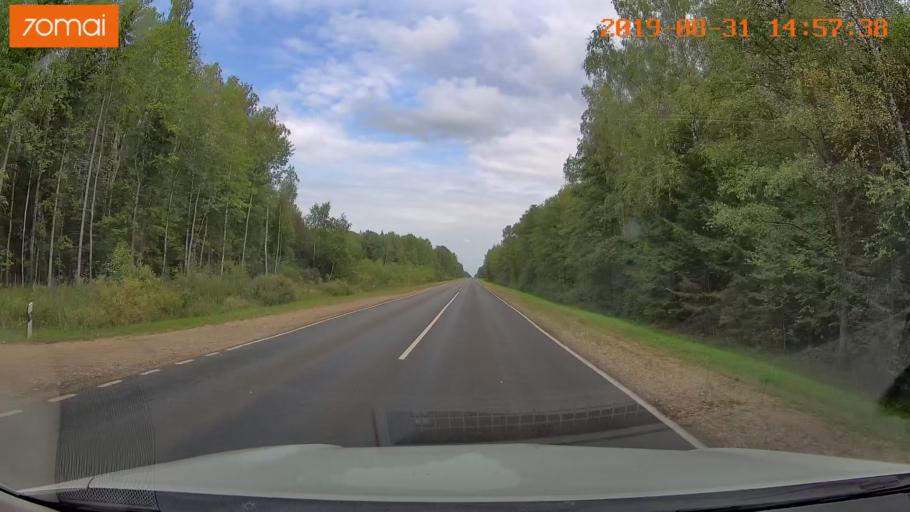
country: RU
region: Kaluga
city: Spas-Demensk
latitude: 54.3118
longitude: 33.9618
